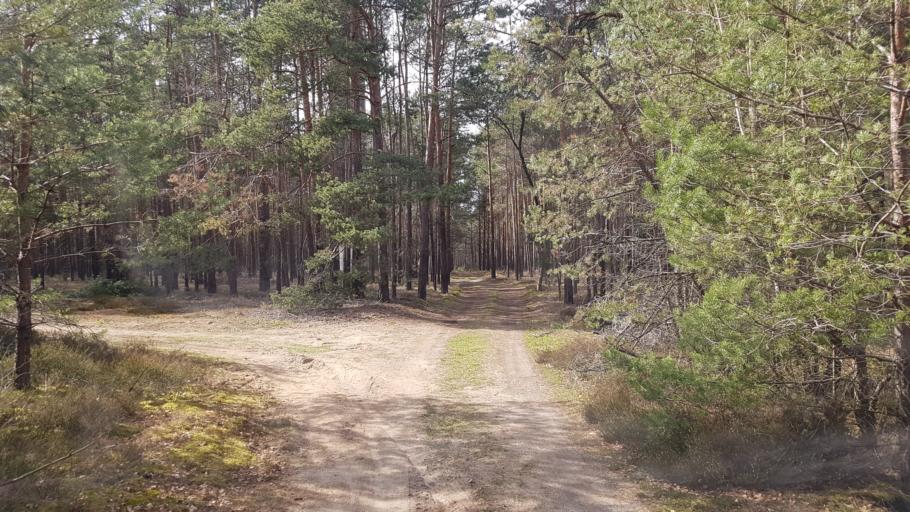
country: DE
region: Brandenburg
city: Schonewalde
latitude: 51.6221
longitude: 13.6317
